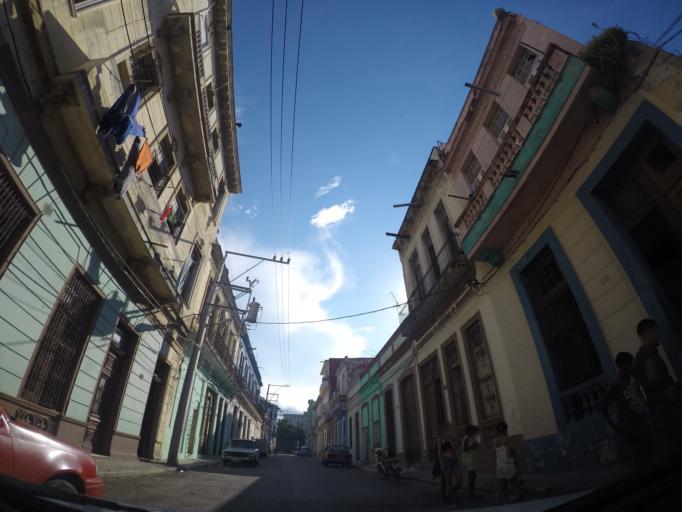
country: CU
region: La Habana
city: Havana
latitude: 23.1402
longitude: -82.3776
